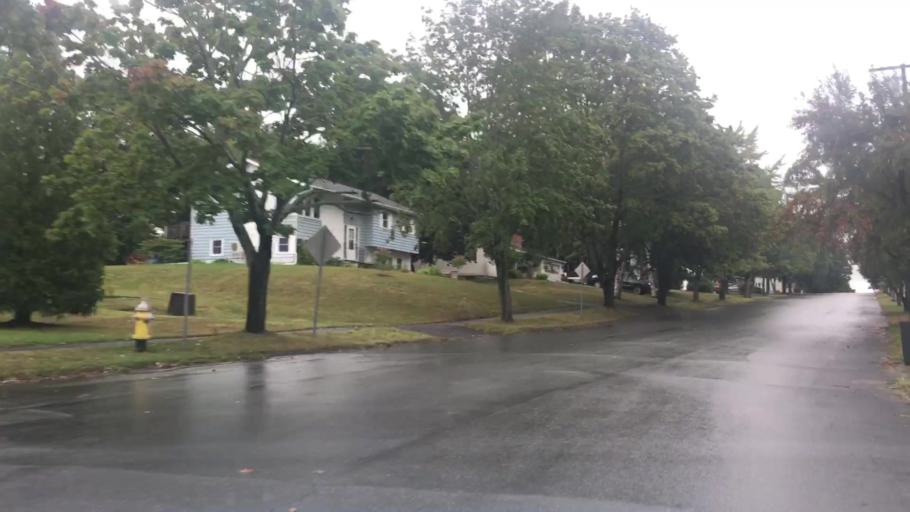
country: US
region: Maine
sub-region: Penobscot County
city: Brewer
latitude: 44.8194
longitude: -68.7611
